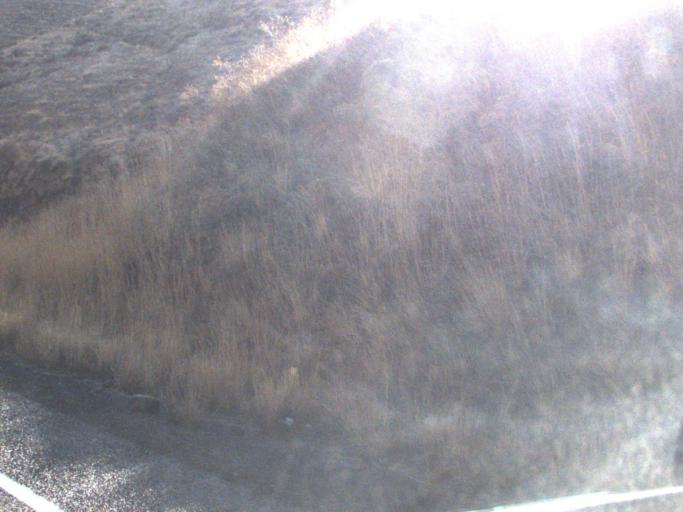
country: US
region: Washington
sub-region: Garfield County
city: Pomeroy
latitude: 46.4375
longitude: -117.3629
